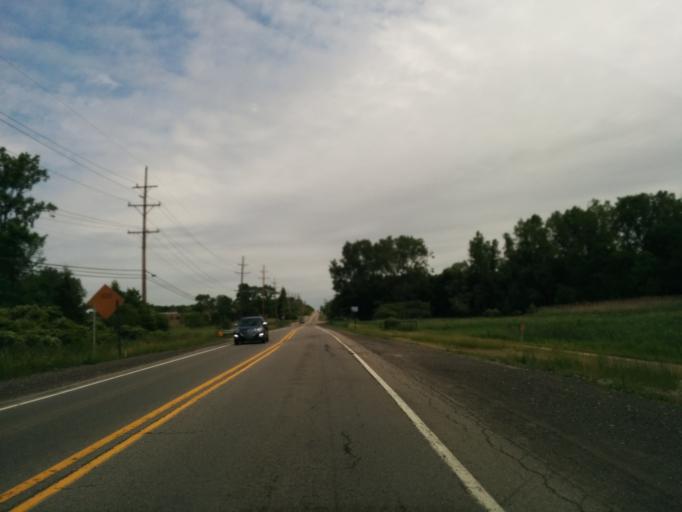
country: US
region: Michigan
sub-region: Oakland County
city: Walled Lake
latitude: 42.5134
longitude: -83.4368
